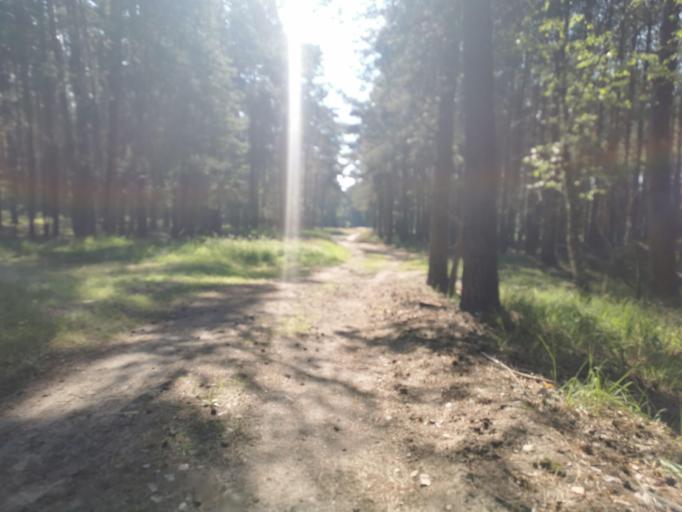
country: SK
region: Trnavsky
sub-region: Okres Senica
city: Senica
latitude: 48.6086
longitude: 17.2731
